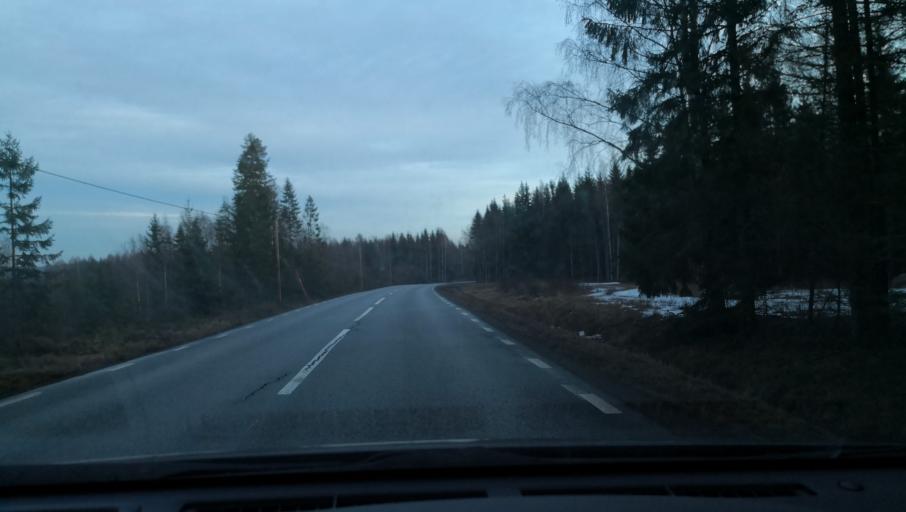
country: SE
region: OErebro
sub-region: Degerfors Kommun
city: Degerfors
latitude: 59.1340
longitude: 14.4692
